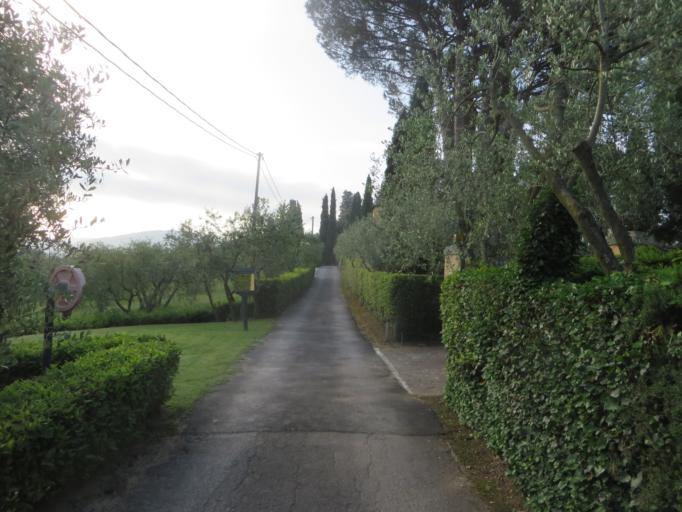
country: IT
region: Tuscany
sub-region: Province of Florence
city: Bagno a Ripoli
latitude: 43.7460
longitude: 11.3188
